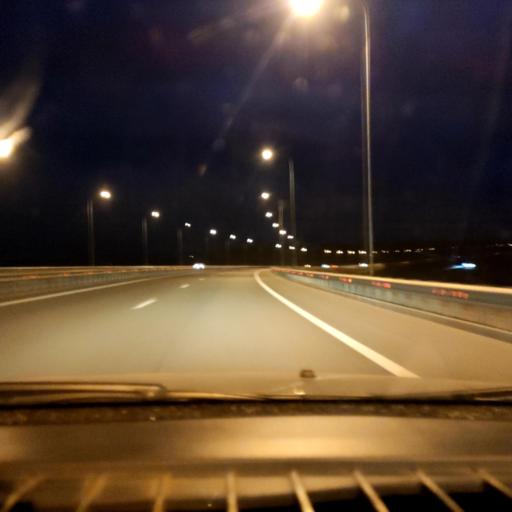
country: RU
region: Samara
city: Bereza
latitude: 53.5015
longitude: 50.1172
